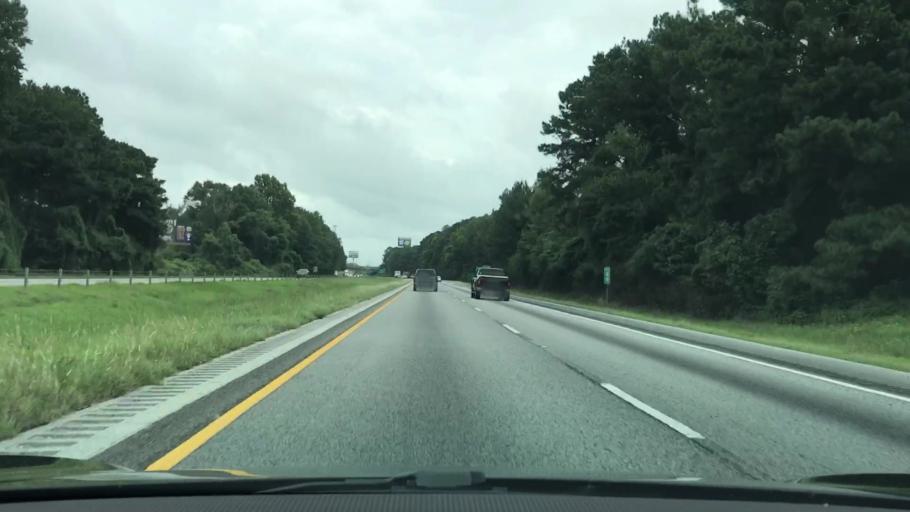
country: US
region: Alabama
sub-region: Lee County
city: Auburn
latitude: 32.5393
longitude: -85.5409
